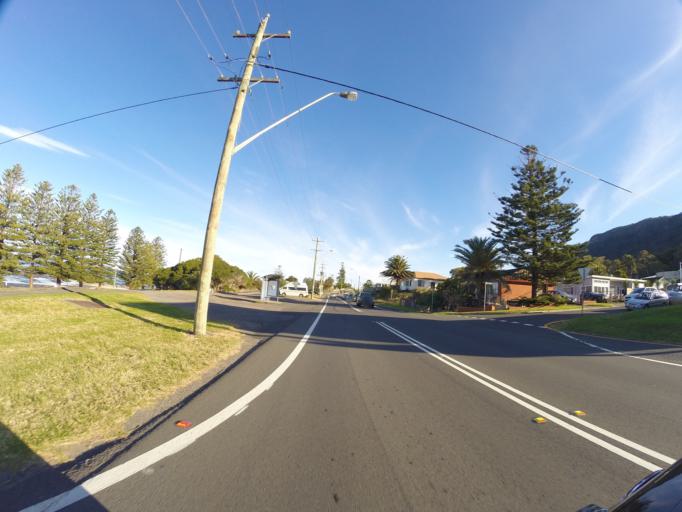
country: AU
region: New South Wales
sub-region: Wollongong
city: Bulli
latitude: -34.2870
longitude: 150.9482
